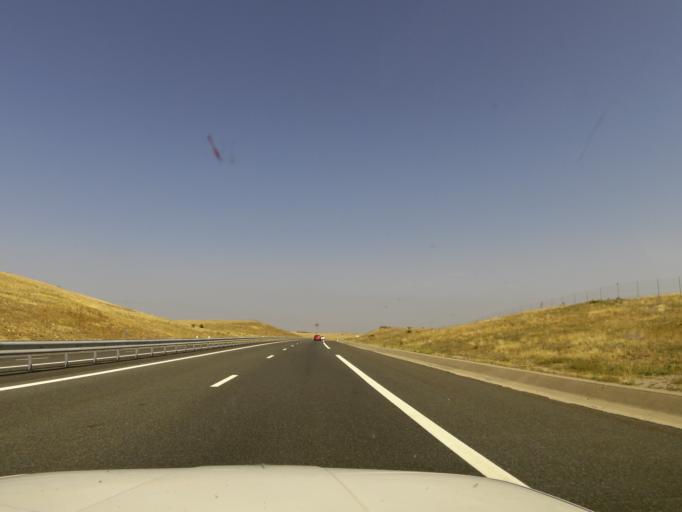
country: FR
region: Midi-Pyrenees
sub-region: Departement de l'Aveyron
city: La Cavalerie
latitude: 44.0272
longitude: 3.1096
